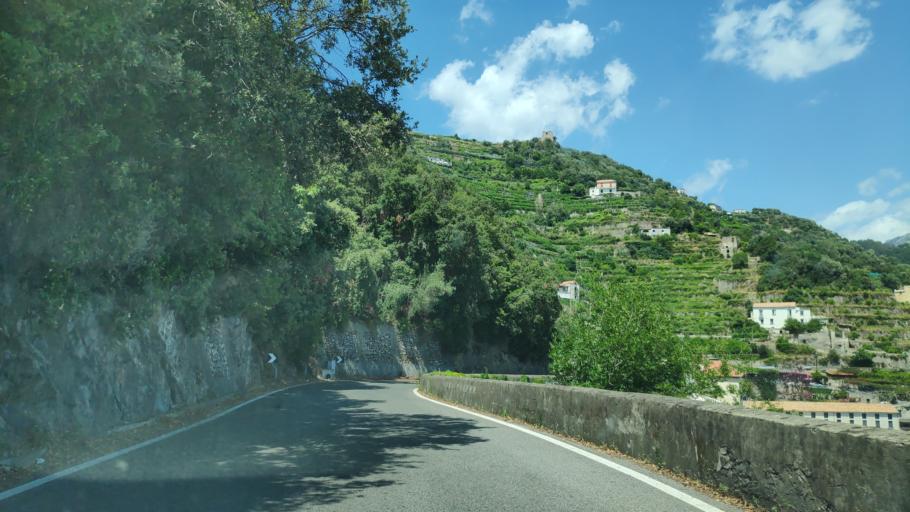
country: IT
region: Campania
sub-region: Provincia di Salerno
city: Ravello
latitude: 40.6445
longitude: 14.6185
